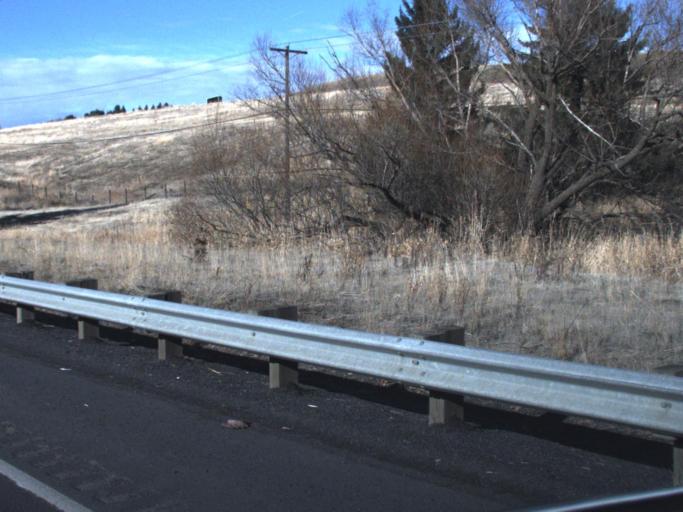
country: US
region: Washington
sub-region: Whitman County
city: Pullman
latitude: 46.7218
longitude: -117.1468
